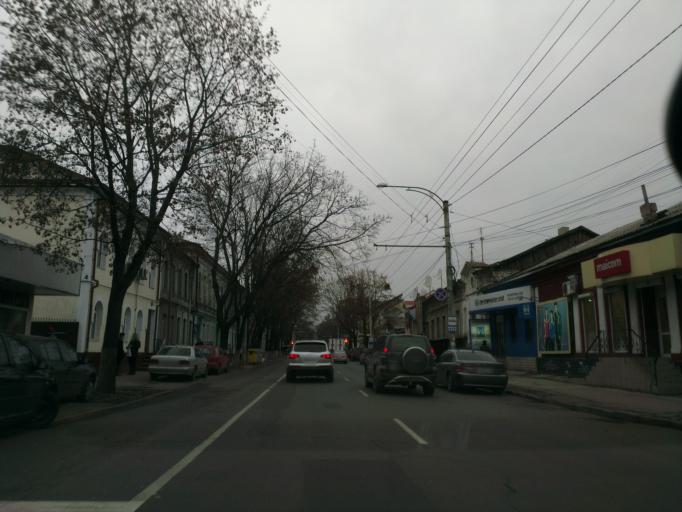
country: MD
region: Chisinau
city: Chisinau
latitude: 47.0169
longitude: 28.8352
